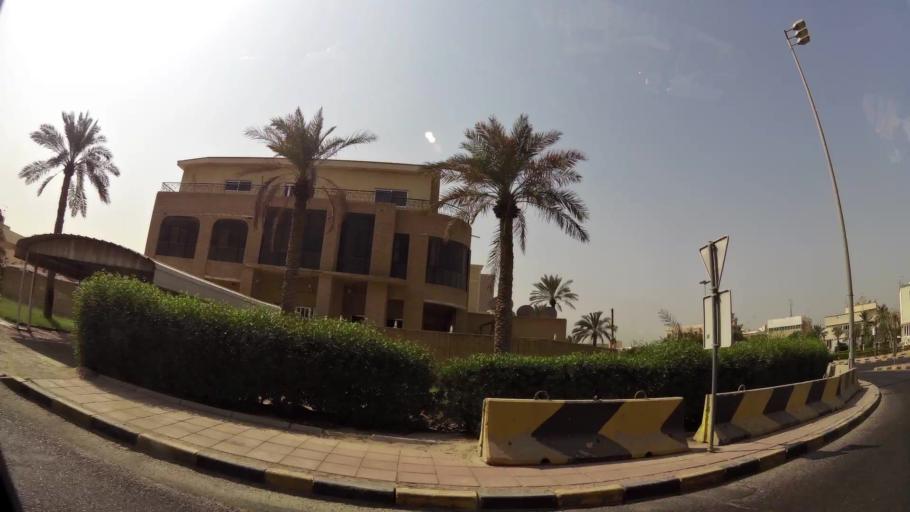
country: KW
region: Al Asimah
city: Ad Dasmah
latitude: 29.3541
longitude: 48.0005
